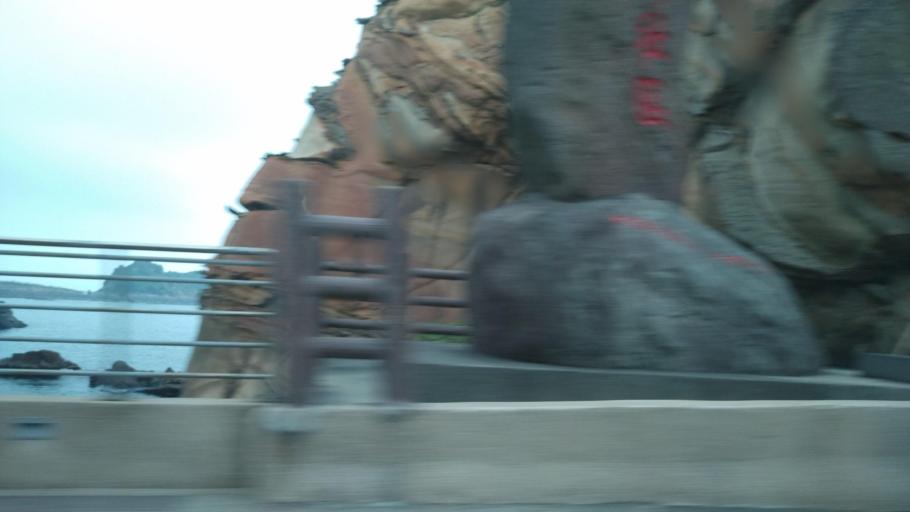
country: TW
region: Taiwan
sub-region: Keelung
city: Keelung
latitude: 25.2029
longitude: 121.6942
